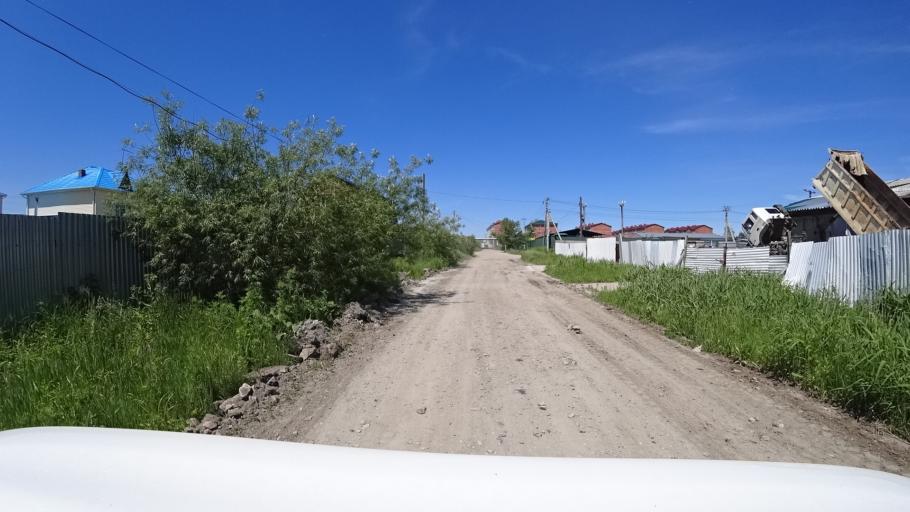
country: RU
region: Khabarovsk Krai
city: Topolevo
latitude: 48.5036
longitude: 135.1789
